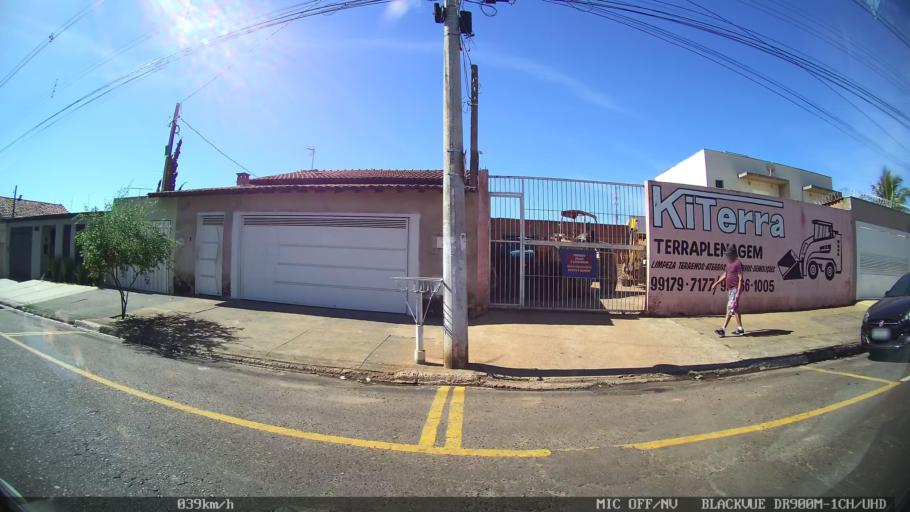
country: BR
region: Sao Paulo
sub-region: Franca
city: Franca
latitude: -20.5589
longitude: -47.3730
